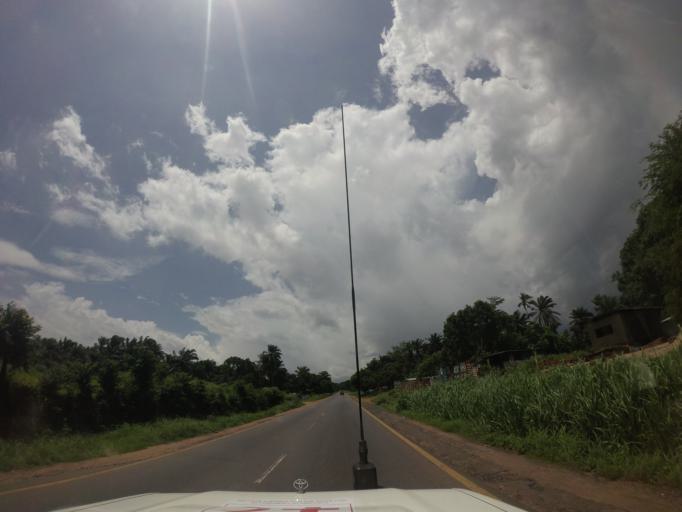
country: SL
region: Western Area
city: Waterloo
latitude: 8.3351
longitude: -13.0183
